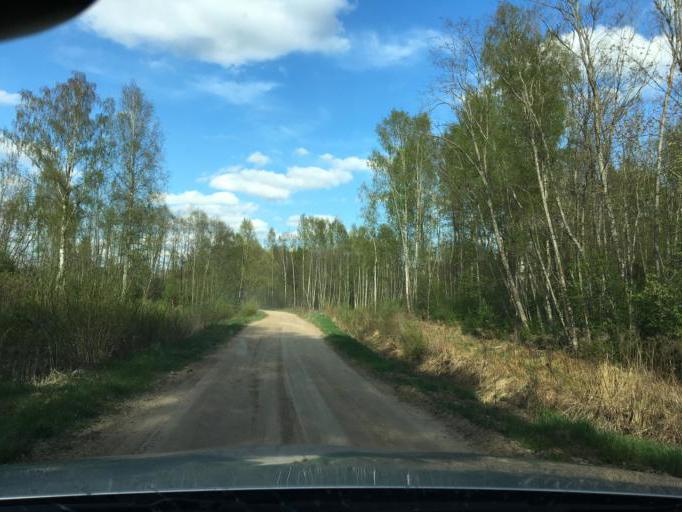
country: LV
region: Ozolnieku
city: Ozolnieki
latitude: 56.6665
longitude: 23.8773
